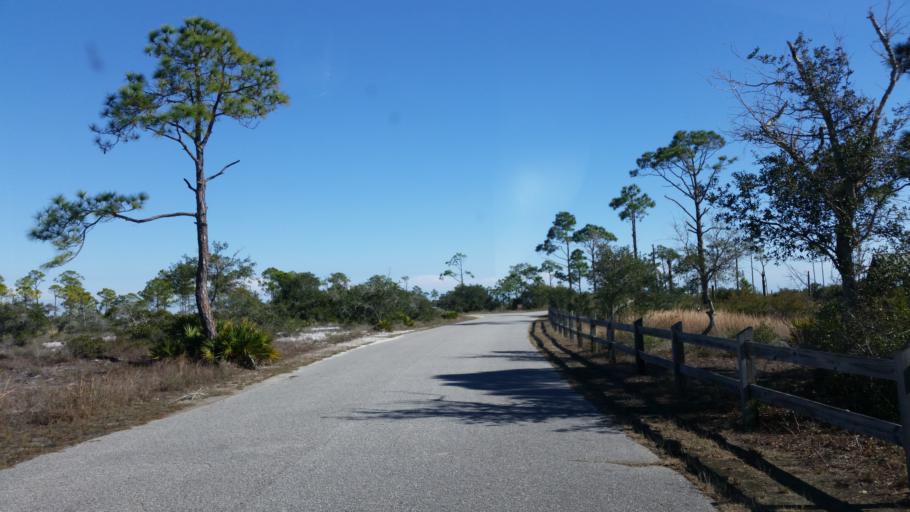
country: US
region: Florida
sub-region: Escambia County
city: Myrtle Grove
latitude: 30.3110
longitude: -87.4062
